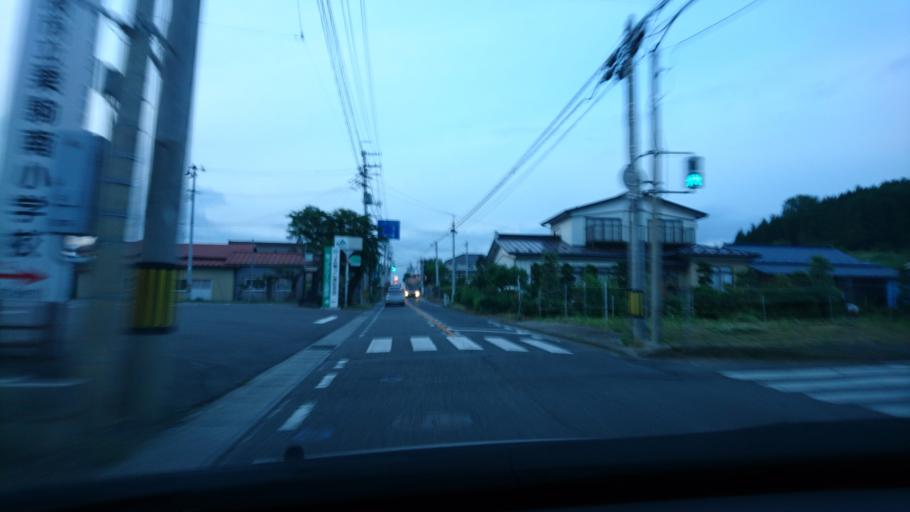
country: JP
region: Iwate
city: Ichinoseki
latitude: 38.8135
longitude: 140.9850
